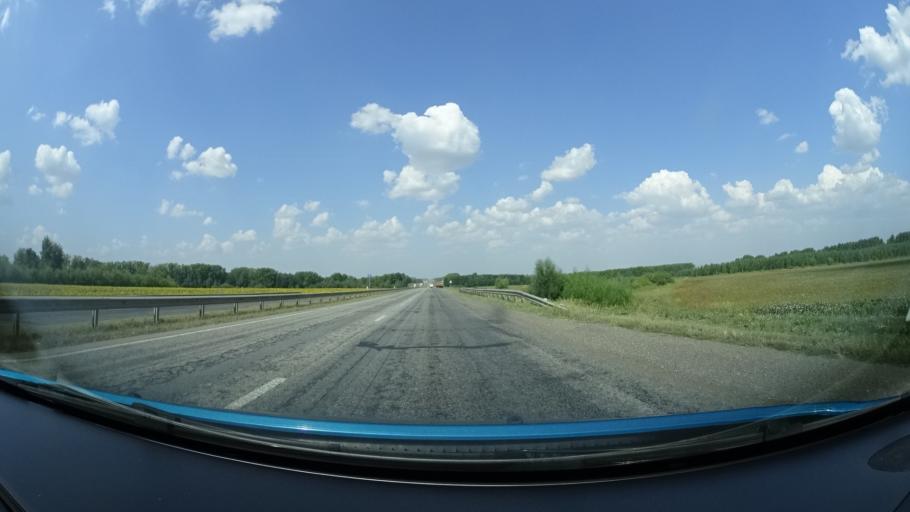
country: RU
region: Bashkortostan
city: Dmitriyevka
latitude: 54.7099
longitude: 55.2205
